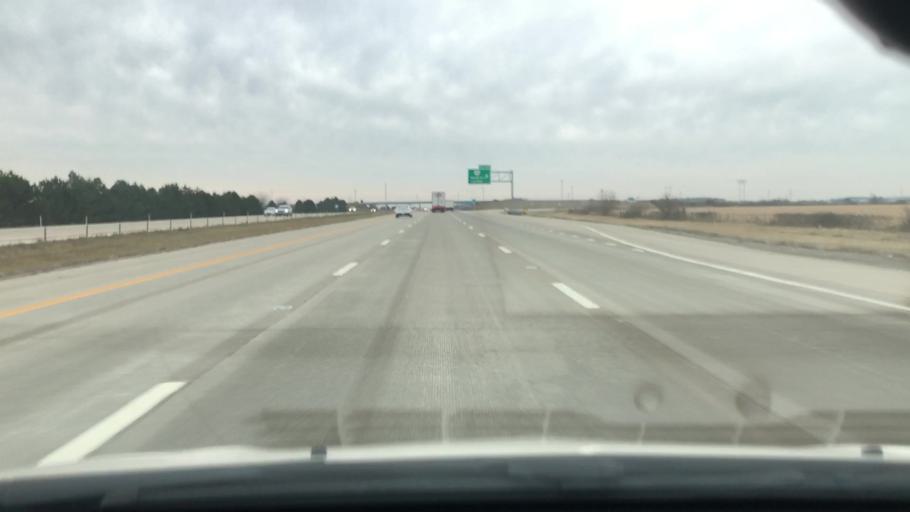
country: US
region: Ohio
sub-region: Wood County
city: Bowling Green
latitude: 41.4523
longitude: -83.6221
